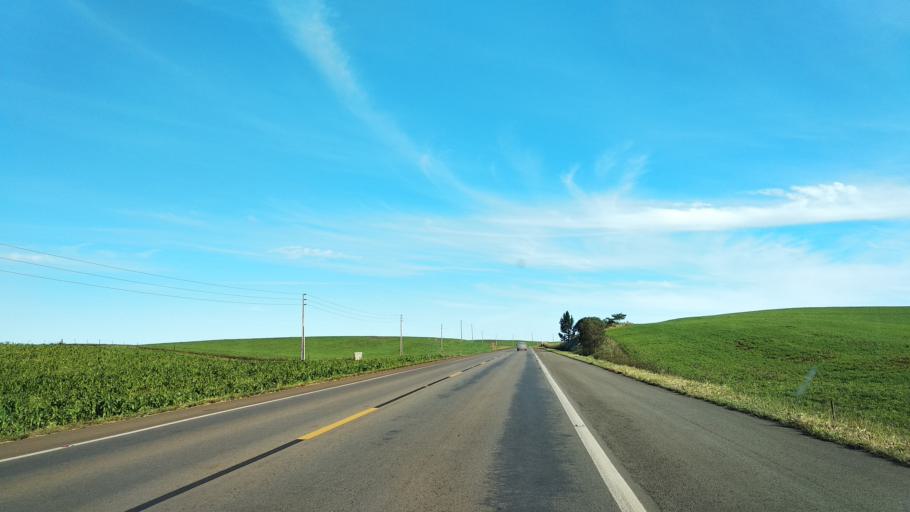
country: BR
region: Santa Catarina
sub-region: Celso Ramos
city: Celso Ramos
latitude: -27.5172
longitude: -51.3503
